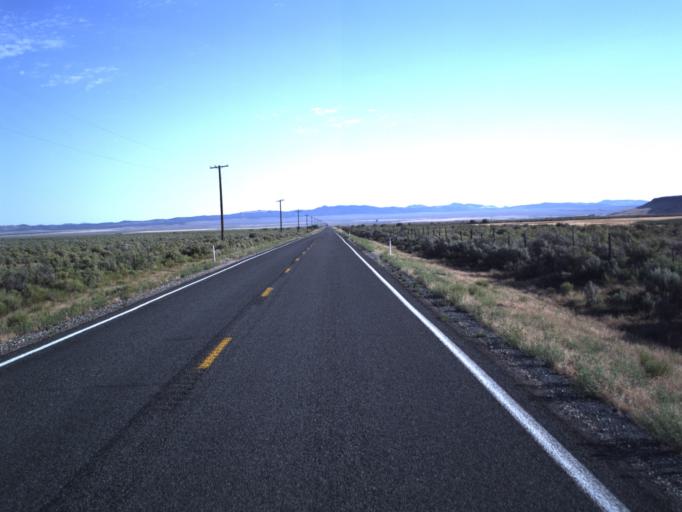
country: US
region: Utah
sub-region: Iron County
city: Enoch
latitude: 37.8121
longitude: -113.0505
